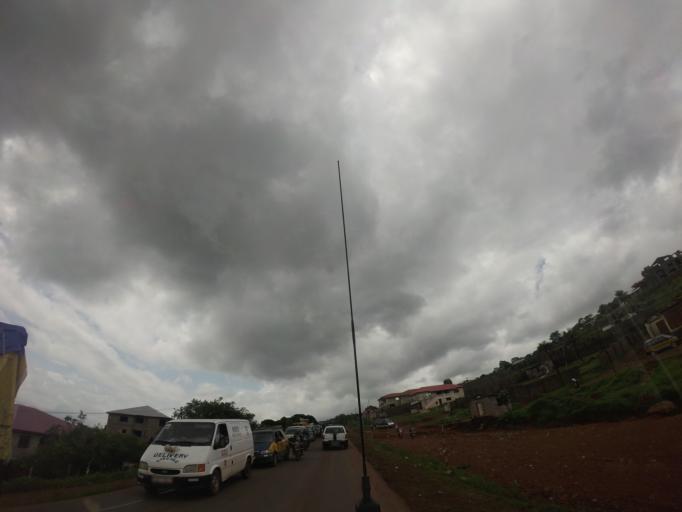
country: SL
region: Western Area
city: Hastings
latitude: 8.3871
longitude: -13.1204
